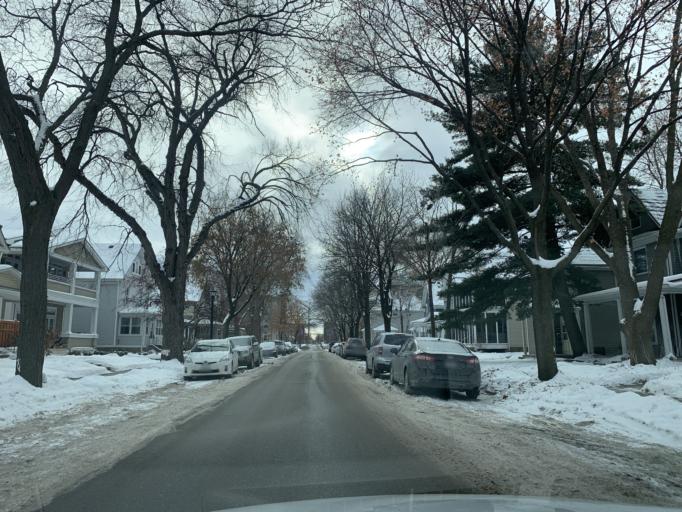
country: US
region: Minnesota
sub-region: Hennepin County
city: Minneapolis
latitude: 44.9530
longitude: -93.2945
